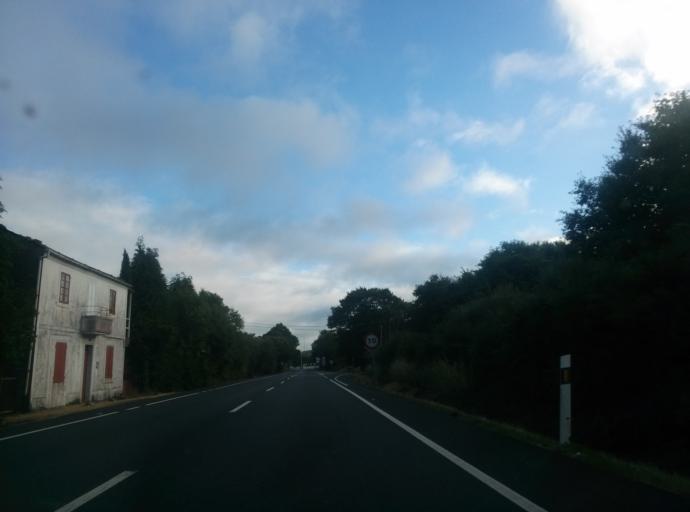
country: ES
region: Galicia
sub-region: Provincia de Lugo
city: Muras
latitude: 43.4038
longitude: -7.7805
